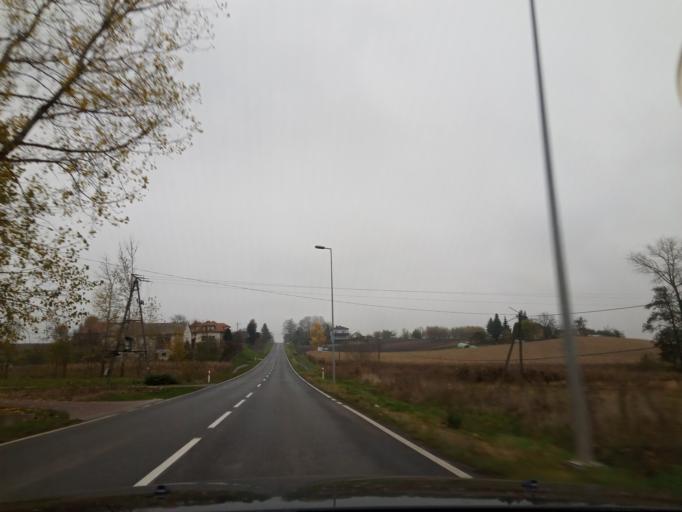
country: PL
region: Lesser Poland Voivodeship
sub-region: Powiat proszowicki
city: Klimontow
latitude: 50.2290
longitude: 20.3233
